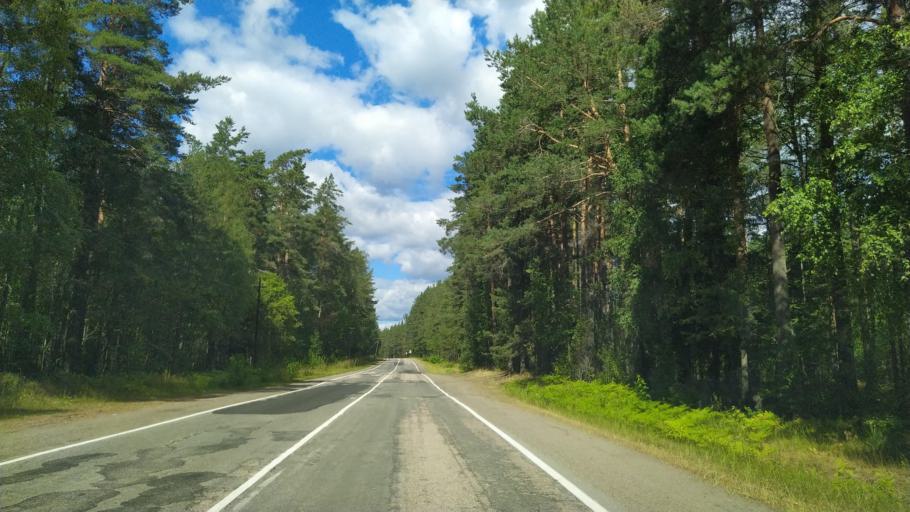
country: RU
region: Leningrad
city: Priozersk
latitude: 60.9987
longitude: 30.2472
